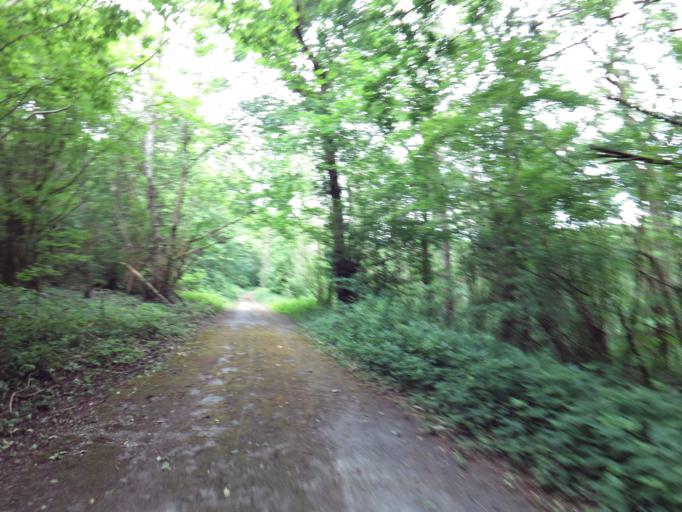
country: IE
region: Connaught
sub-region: County Galway
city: Gort
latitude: 53.0768
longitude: -8.8678
